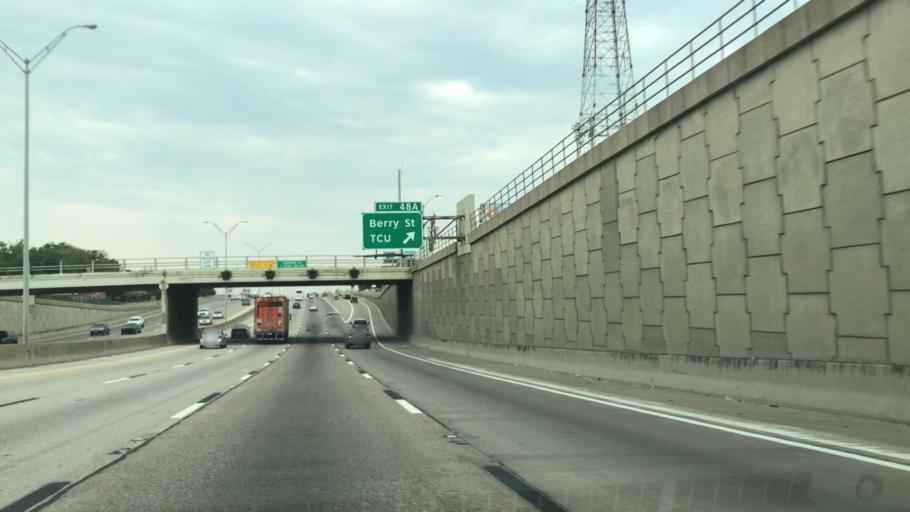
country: US
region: Texas
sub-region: Tarrant County
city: Fort Worth
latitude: 32.7140
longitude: -97.3207
